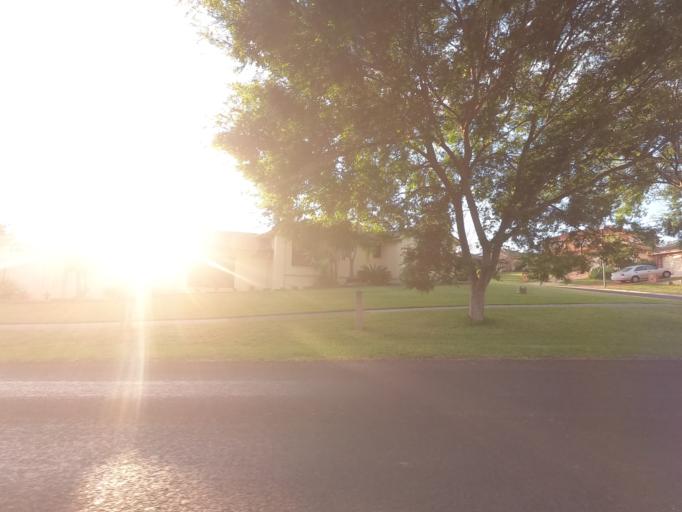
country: AU
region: New South Wales
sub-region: Wollongong
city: Dapto
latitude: -34.4904
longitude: 150.7696
